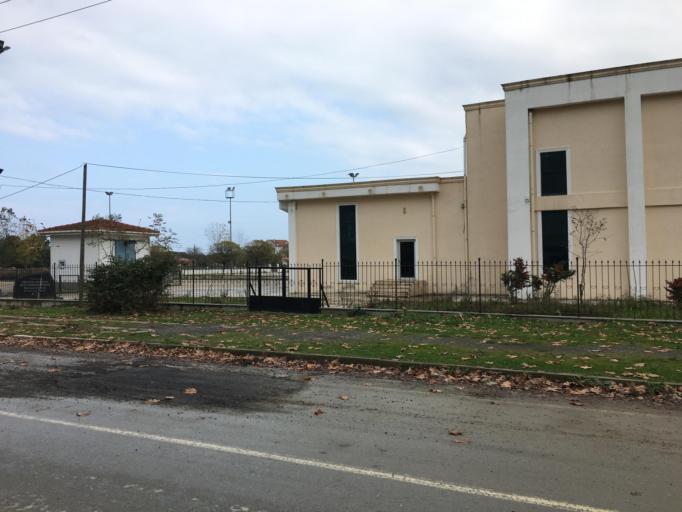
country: TR
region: Samsun
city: Alacam
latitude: 41.6313
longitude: 35.6093
